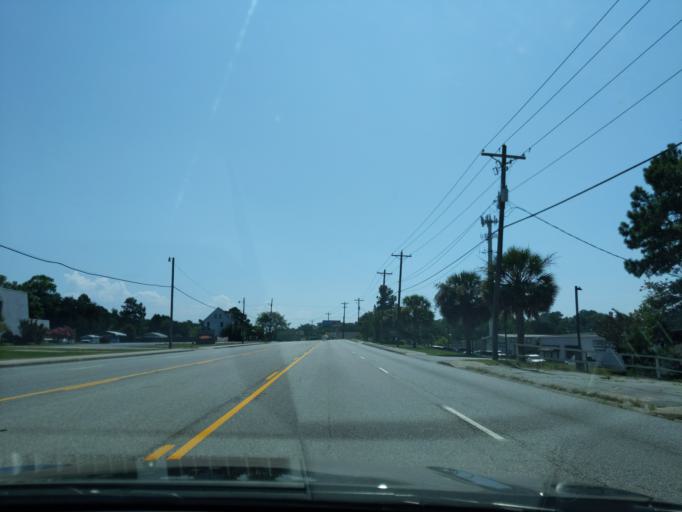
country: US
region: South Carolina
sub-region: Lexington County
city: Oak Grove
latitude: 33.9722
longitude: -81.1477
